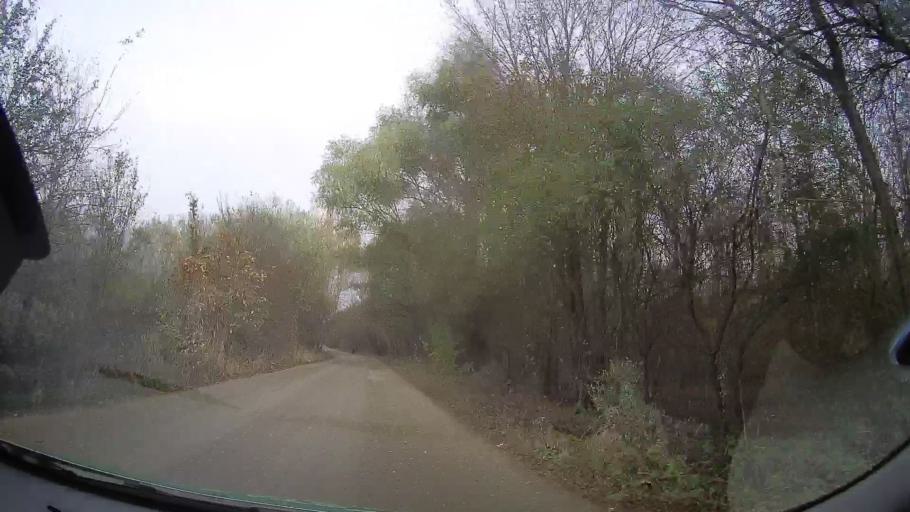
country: RO
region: Ialomita
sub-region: Comuna Fierbinti-Targ
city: Fierbinti-Targ
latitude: 44.6816
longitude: 26.3483
